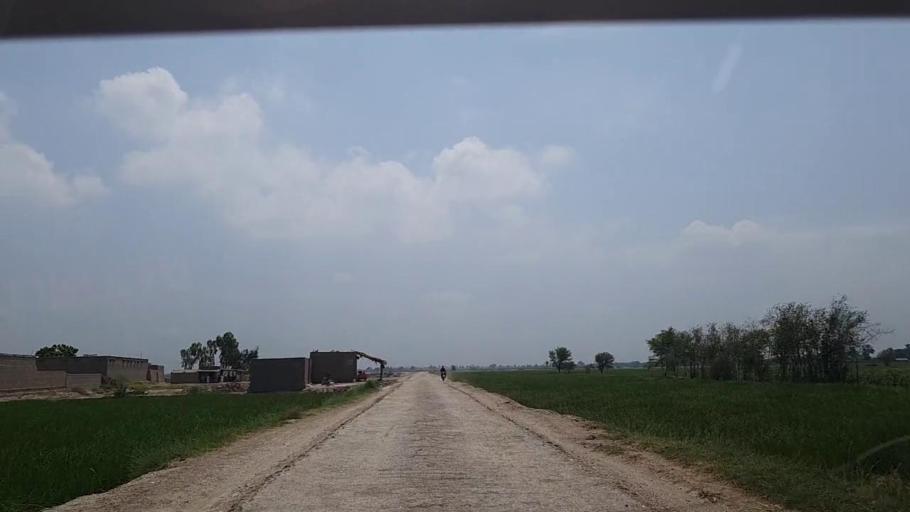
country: PK
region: Sindh
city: Khanpur
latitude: 27.9036
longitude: 69.3915
